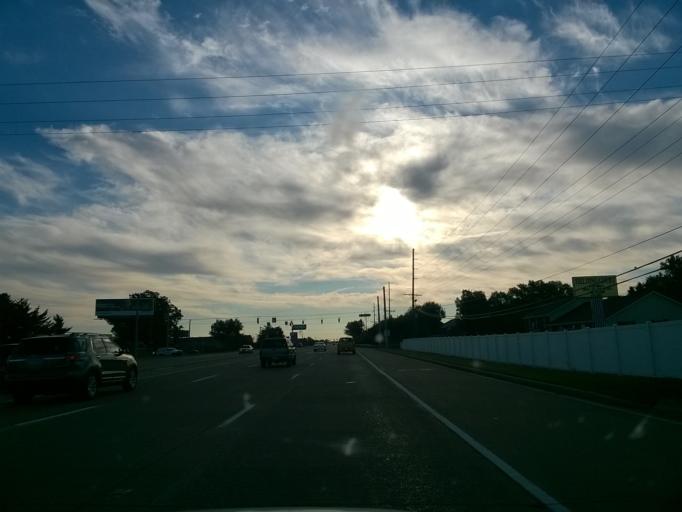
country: US
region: Indiana
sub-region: Vanderburgh County
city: Melody Hill
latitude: 37.9766
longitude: -87.4805
